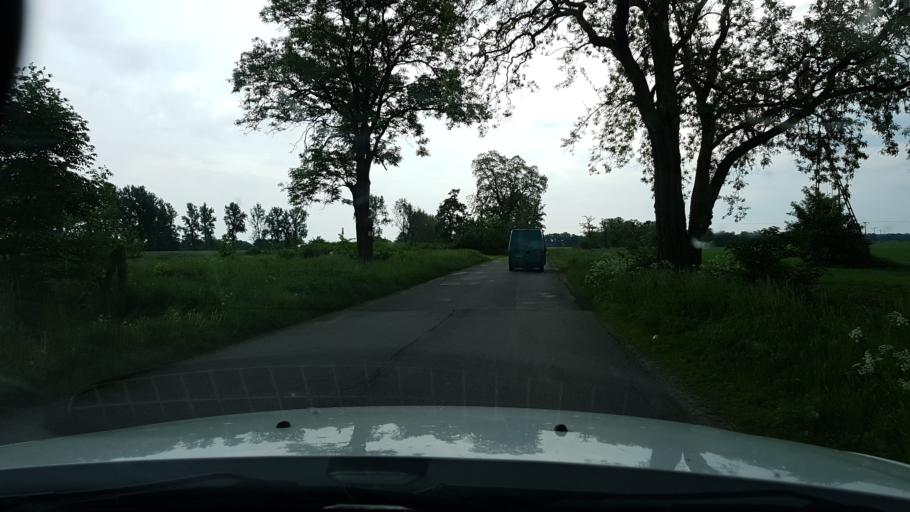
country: PL
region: West Pomeranian Voivodeship
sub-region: Powiat stargardzki
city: Marianowo
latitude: 53.3173
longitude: 15.1782
